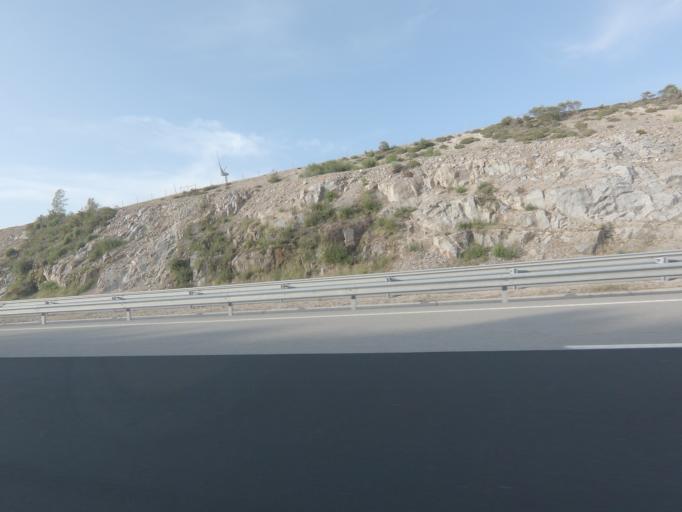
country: PT
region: Vila Real
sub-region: Vila Pouca de Aguiar
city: Vila Pouca de Aguiar
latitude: 41.4422
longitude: -7.6451
